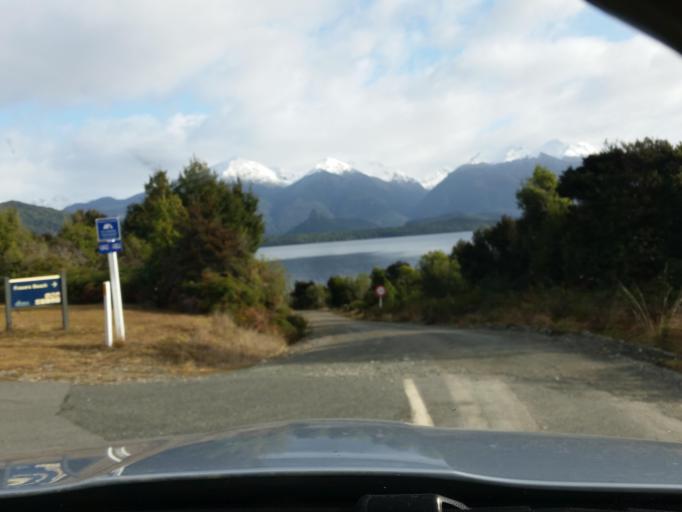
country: NZ
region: Southland
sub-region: Southland District
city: Te Anau
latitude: -45.5552
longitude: 167.6237
